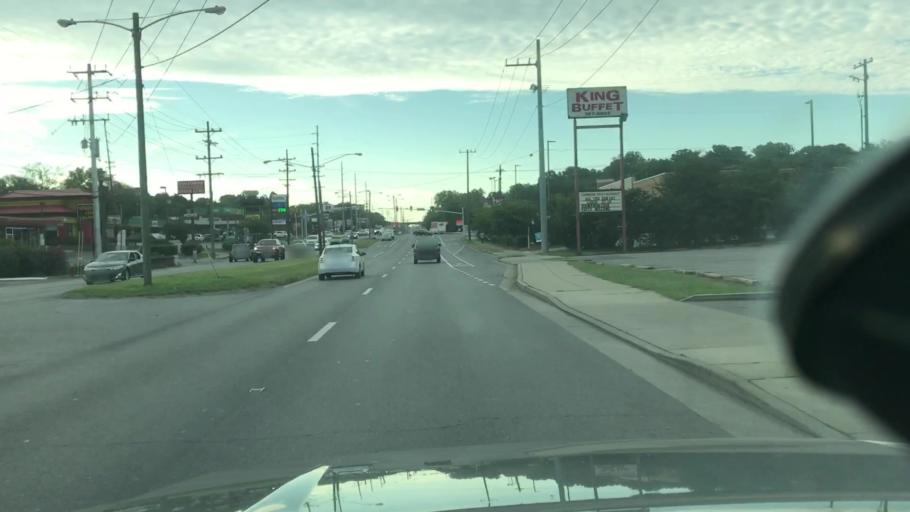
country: US
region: Tennessee
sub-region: Davidson County
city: Oak Hill
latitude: 36.1278
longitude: -86.7127
